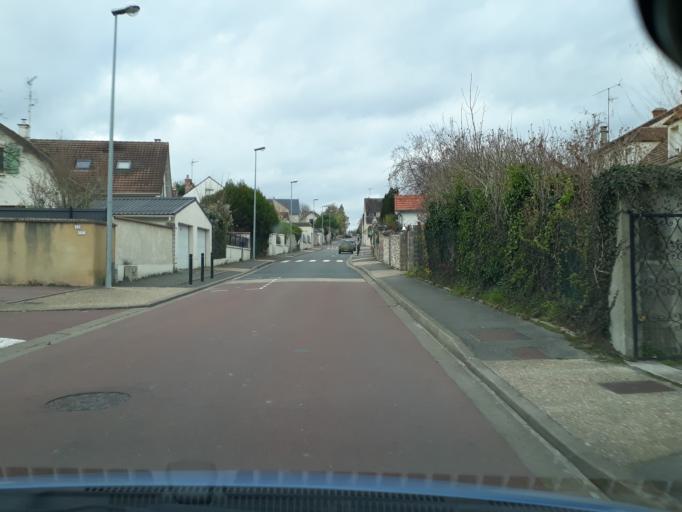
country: FR
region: Ile-de-France
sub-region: Departement de Seine-et-Marne
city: Veneux-les-Sablons
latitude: 48.3822
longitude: 2.7862
